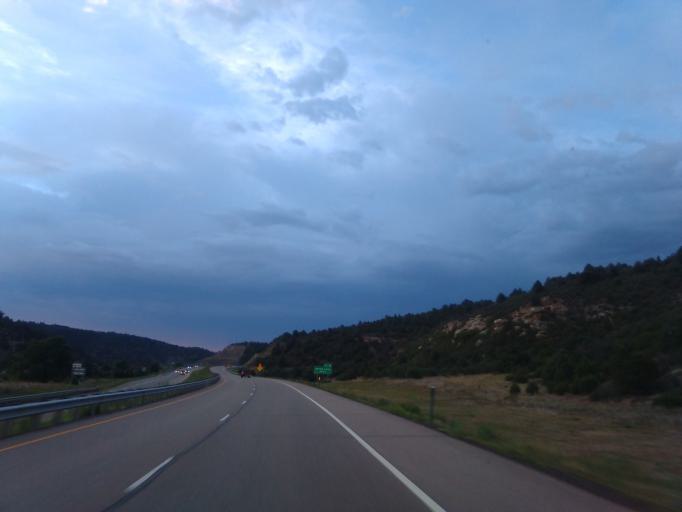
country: US
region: Colorado
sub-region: Las Animas County
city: Trinidad
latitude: 37.0736
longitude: -104.5174
